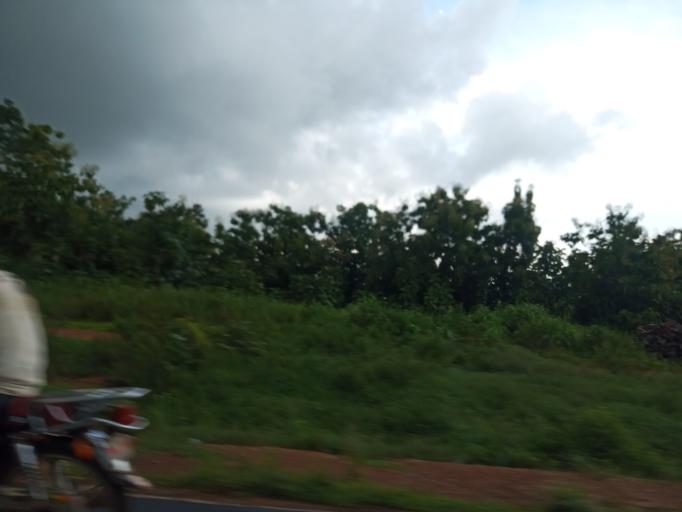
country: TG
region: Centrale
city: Sotouboua
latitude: 8.5955
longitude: 0.9970
